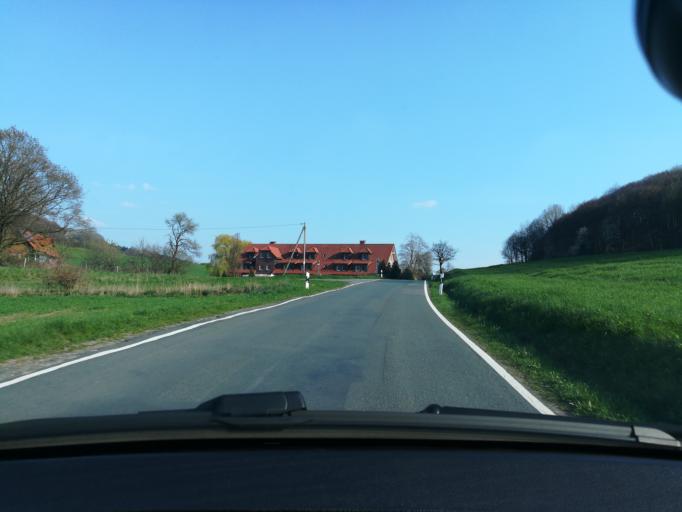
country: DE
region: North Rhine-Westphalia
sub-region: Regierungsbezirk Detmold
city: Werther
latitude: 52.0476
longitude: 8.4008
